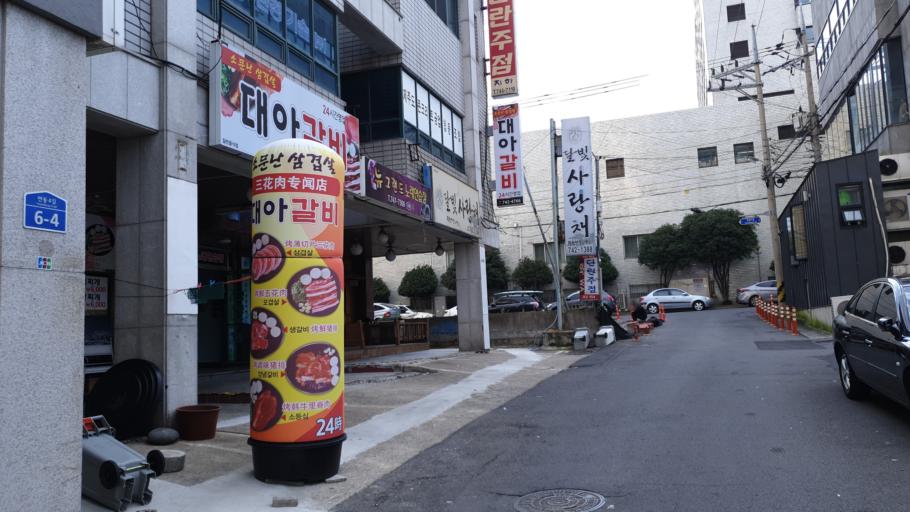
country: KR
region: Jeju-do
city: Jeju-si
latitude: 33.4853
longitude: 126.4875
